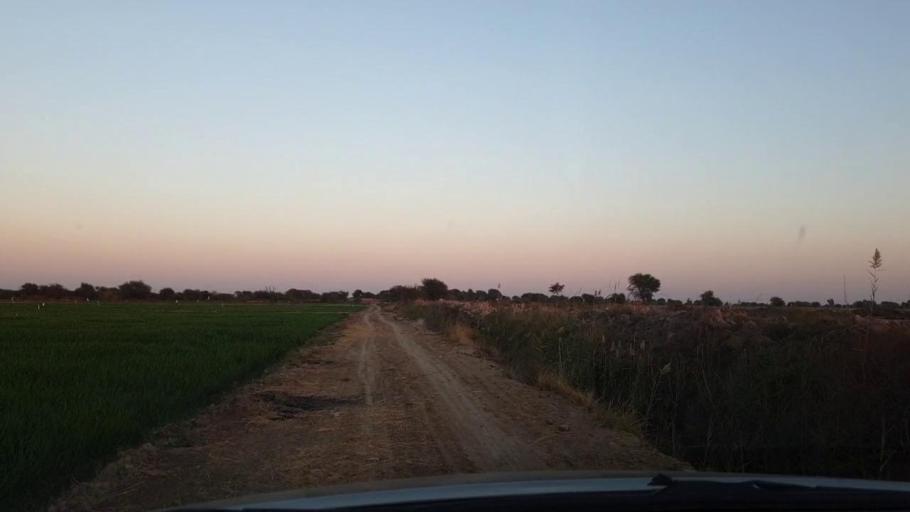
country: PK
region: Sindh
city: Tando Mittha Khan
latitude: 25.8565
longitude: 69.2046
